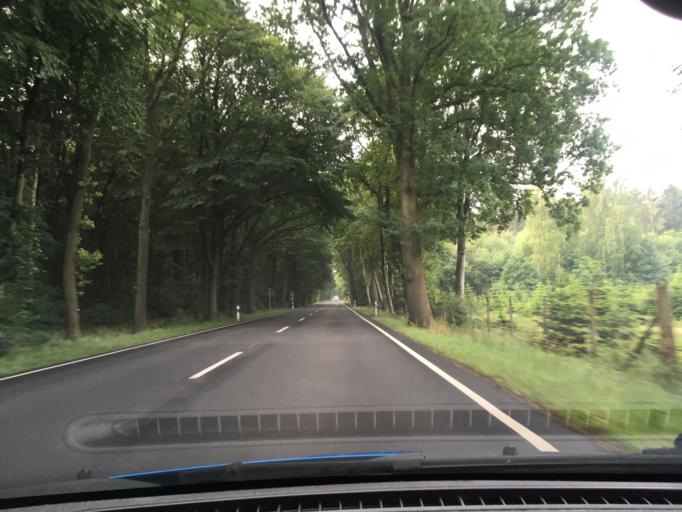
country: DE
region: Lower Saxony
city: Wenzendorf
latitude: 53.3558
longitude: 9.8078
